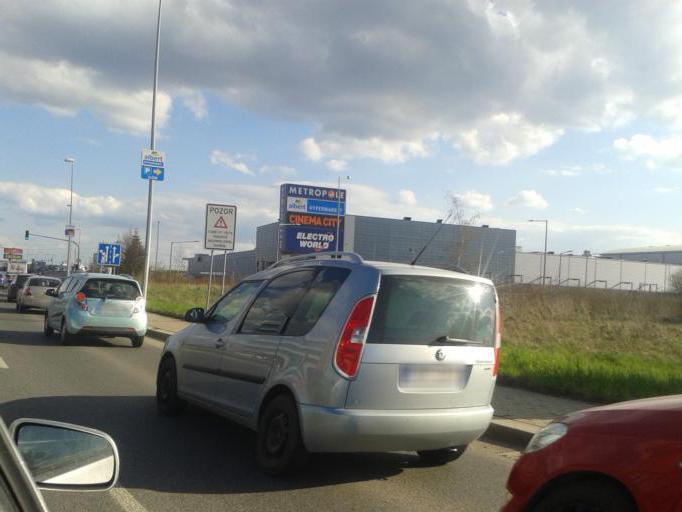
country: CZ
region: Central Bohemia
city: Hostivice
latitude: 50.0559
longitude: 14.2879
